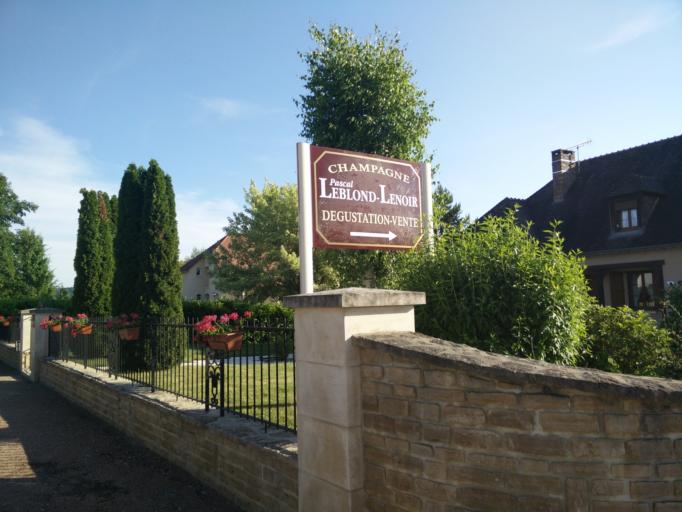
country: FR
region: Champagne-Ardenne
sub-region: Departement de l'Aube
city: Bar-sur-Seine
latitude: 48.0582
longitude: 4.3944
